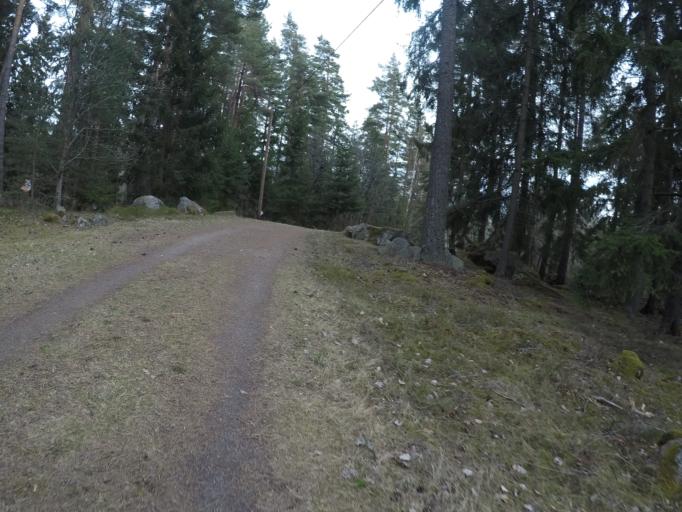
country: SE
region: Soedermanland
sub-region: Eskilstuna Kommun
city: Torshalla
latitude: 59.4233
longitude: 16.4956
